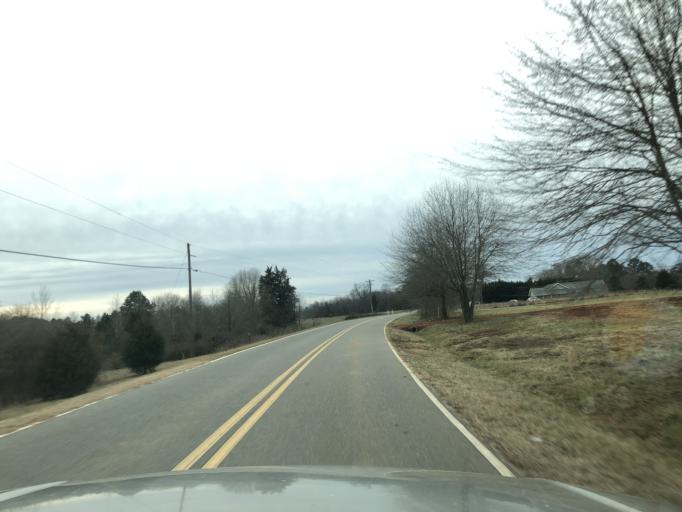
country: US
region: North Carolina
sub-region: Cleveland County
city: Shelby
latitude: 35.3422
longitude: -81.5281
